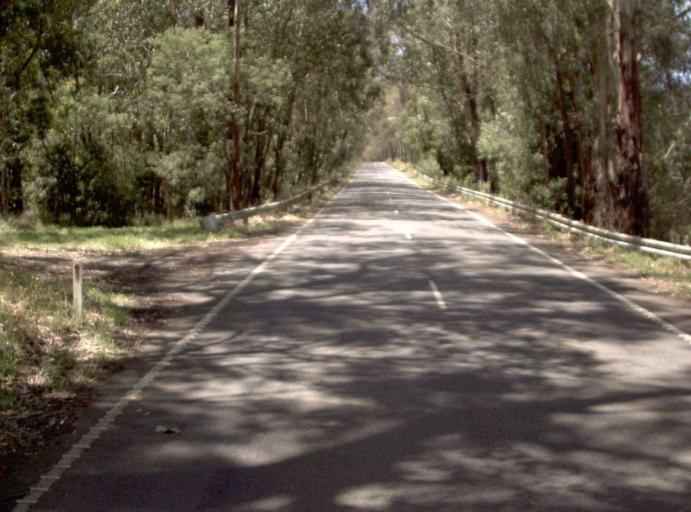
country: AU
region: Victoria
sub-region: Baw Baw
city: Warragul
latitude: -38.0718
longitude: 145.9080
